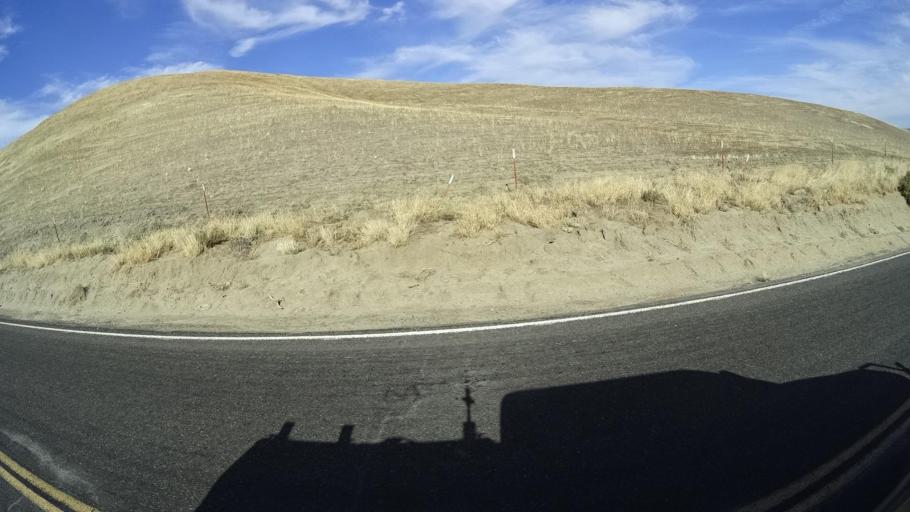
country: US
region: California
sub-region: Kern County
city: Oildale
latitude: 35.6123
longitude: -118.8835
